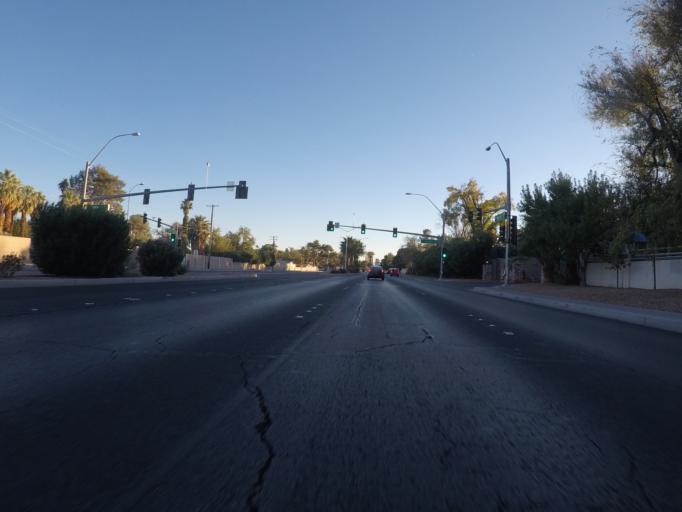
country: US
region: Nevada
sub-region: Clark County
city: Las Vegas
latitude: 36.1684
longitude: -115.1727
